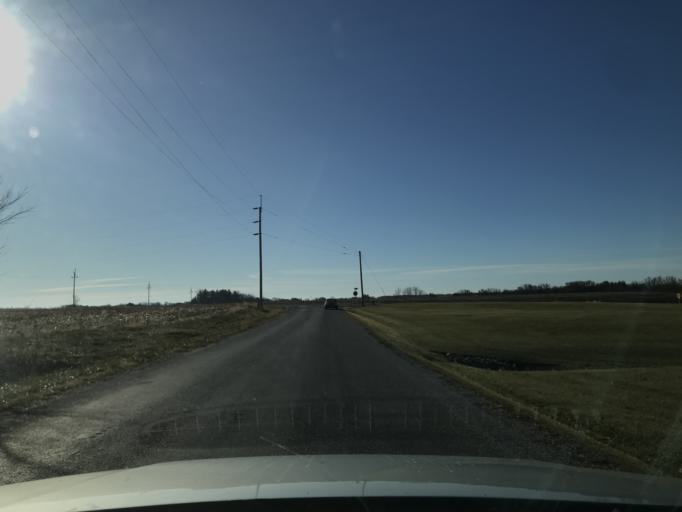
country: US
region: Illinois
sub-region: Hancock County
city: Carthage
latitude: 40.4623
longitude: -91.1784
